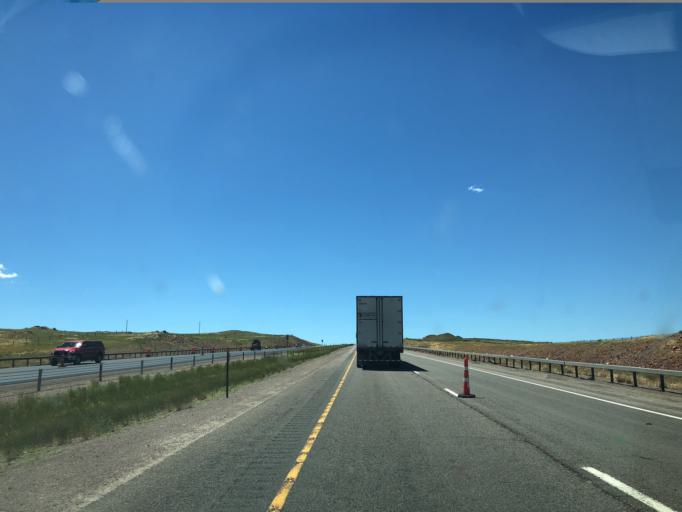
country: US
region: Wyoming
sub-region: Laramie County
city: Cheyenne
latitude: 41.0973
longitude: -105.1730
